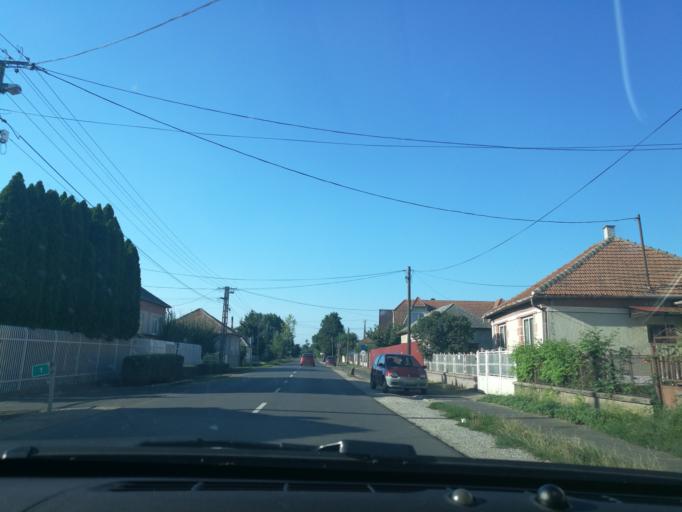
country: HU
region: Szabolcs-Szatmar-Bereg
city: Rakamaz
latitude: 48.1324
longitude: 21.4590
